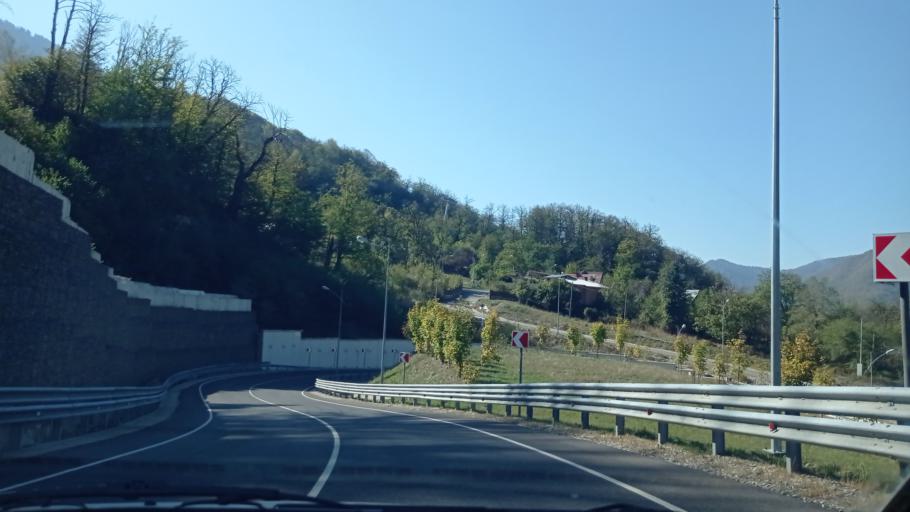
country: RU
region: Krasnodarskiy
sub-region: Sochi City
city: Krasnaya Polyana
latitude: 43.6813
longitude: 40.2433
